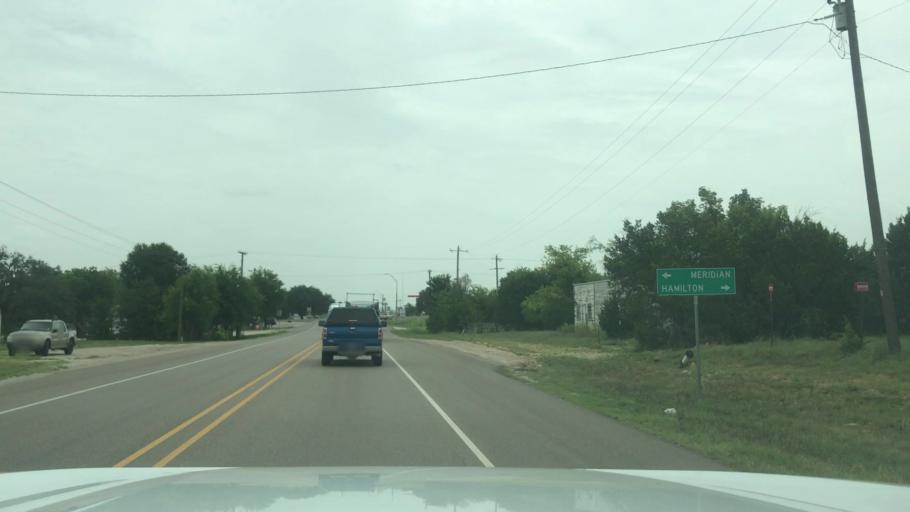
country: US
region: Texas
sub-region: Bosque County
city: Meridian
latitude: 31.9172
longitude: -97.6684
